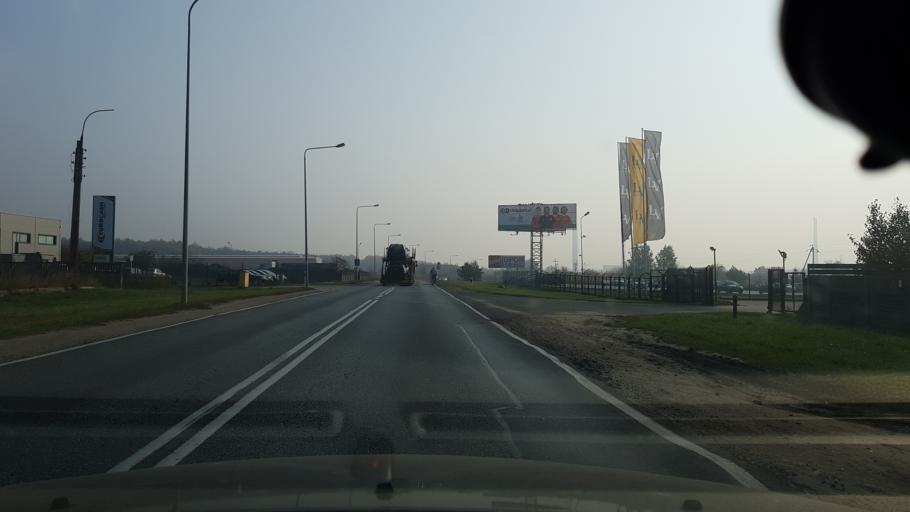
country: PL
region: Lodz Voivodeship
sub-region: Powiat tomaszowski
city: Tomaszow Mazowiecki
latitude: 51.5561
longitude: 20.0222
